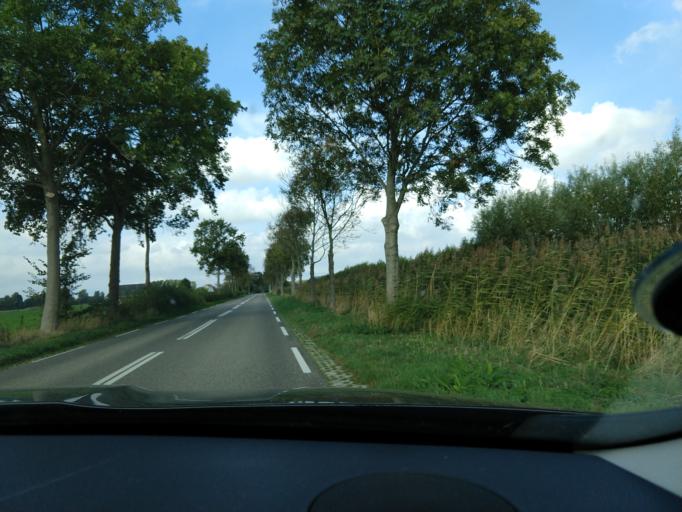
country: NL
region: Zeeland
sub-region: Schouwen-Duiveland
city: Bruinisse
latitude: 51.6655
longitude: 4.0428
